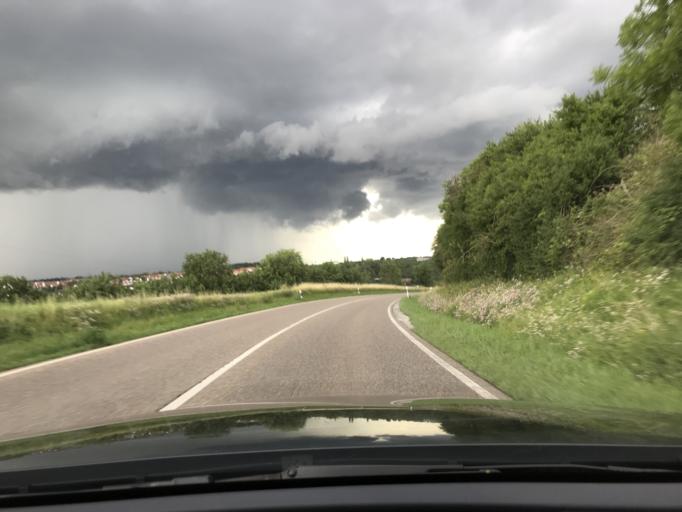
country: DE
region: Baden-Wuerttemberg
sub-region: Regierungsbezirk Stuttgart
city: Stuttgart Muehlhausen
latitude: 48.8626
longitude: 9.2643
